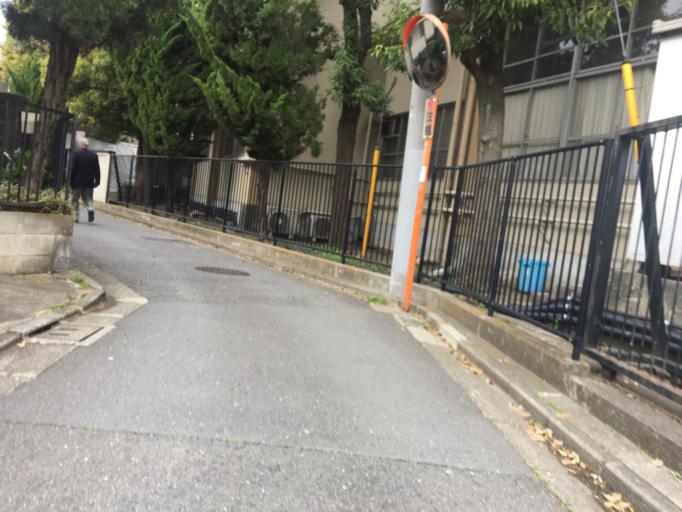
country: JP
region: Tokyo
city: Tokyo
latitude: 35.7167
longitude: 139.6553
